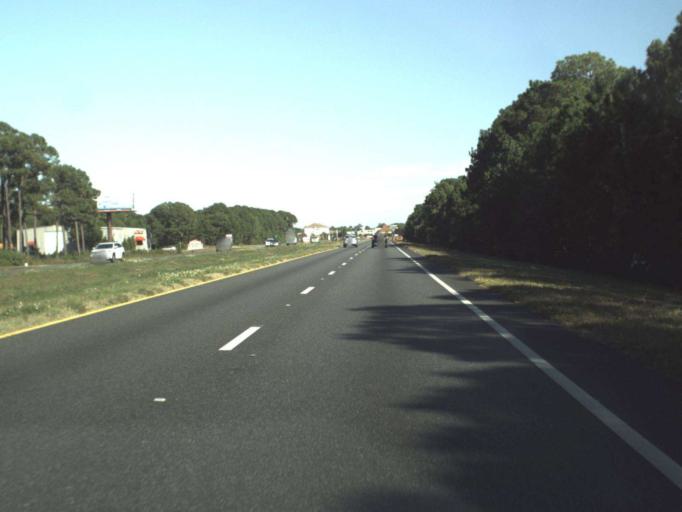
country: US
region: Florida
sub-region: Walton County
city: Miramar Beach
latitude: 30.3848
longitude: -86.3729
